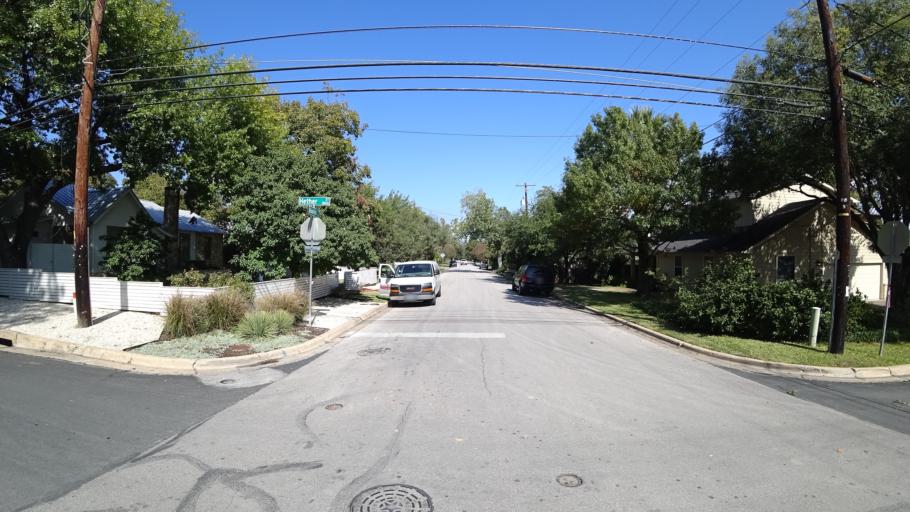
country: US
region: Texas
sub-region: Travis County
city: Rollingwood
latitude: 30.2516
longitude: -97.7715
